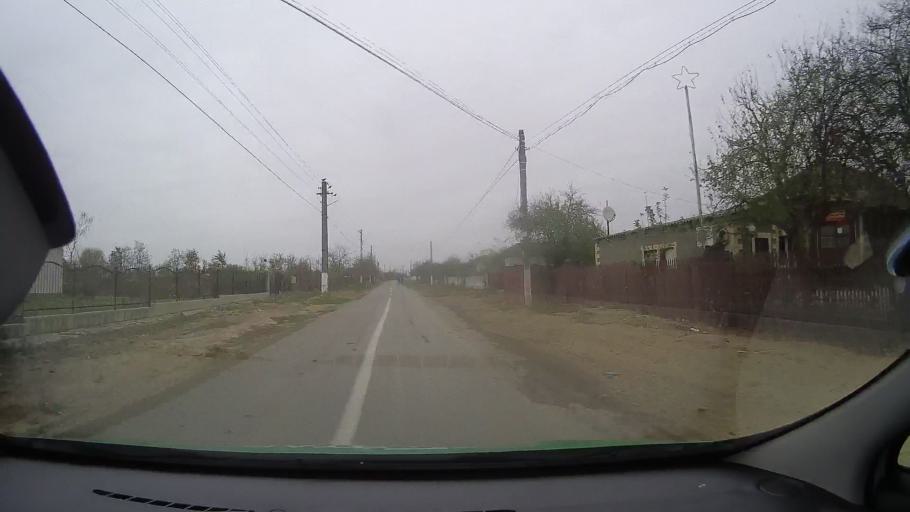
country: RO
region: Constanta
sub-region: Comuna Vulturu
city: Vulturu
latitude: 44.6491
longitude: 28.2689
